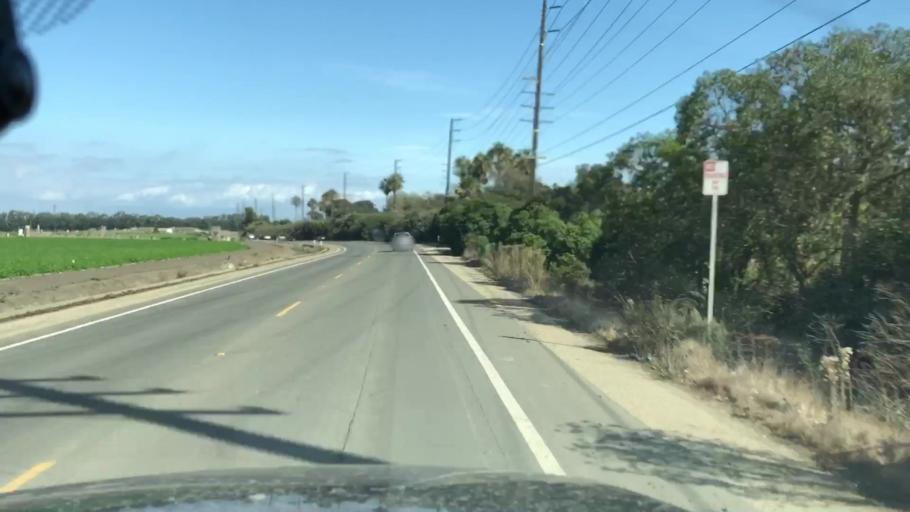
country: US
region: California
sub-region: Ventura County
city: Oxnard Shores
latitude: 34.2431
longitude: -119.2498
